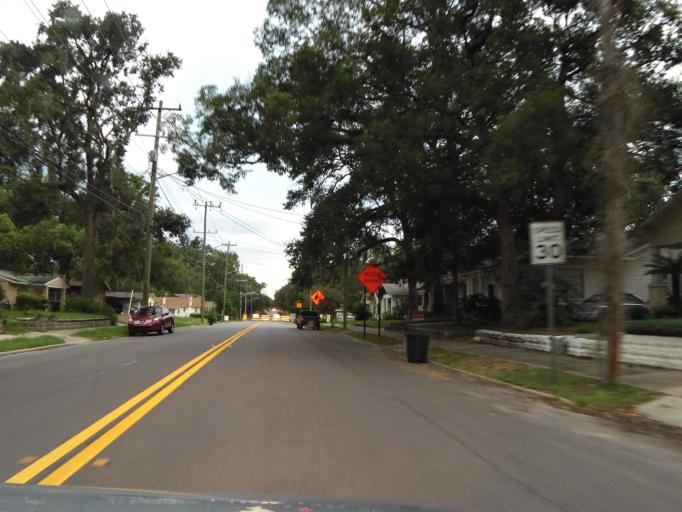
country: US
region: Florida
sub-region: Duval County
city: Jacksonville
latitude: 30.2942
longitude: -81.7110
